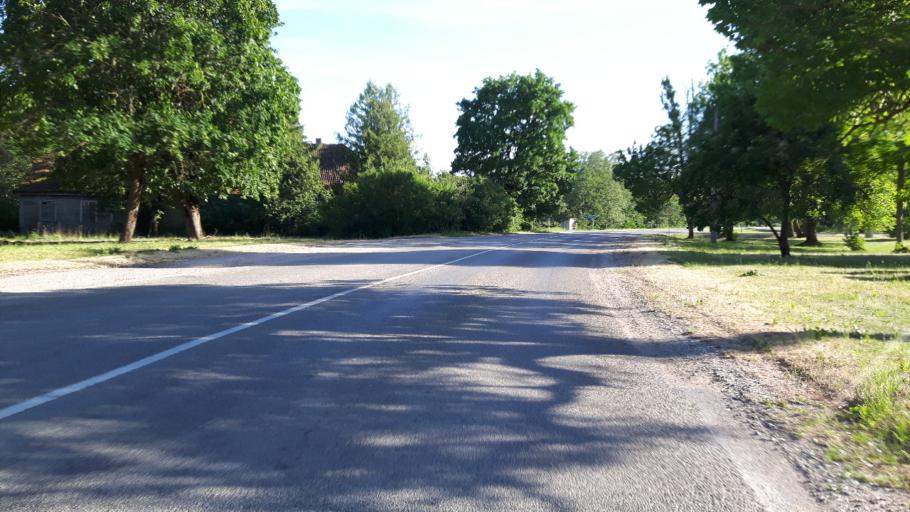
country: LV
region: Talsu Rajons
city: Stende
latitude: 57.0674
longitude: 22.2932
